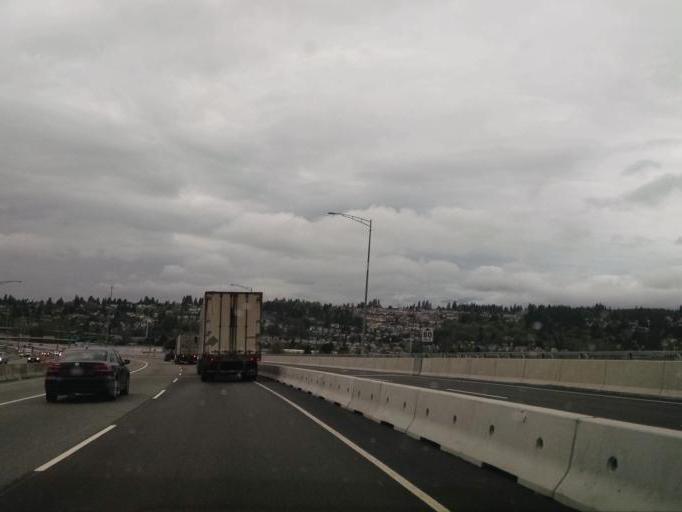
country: CA
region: British Columbia
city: Port Moody
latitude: 49.2256
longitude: -122.8170
